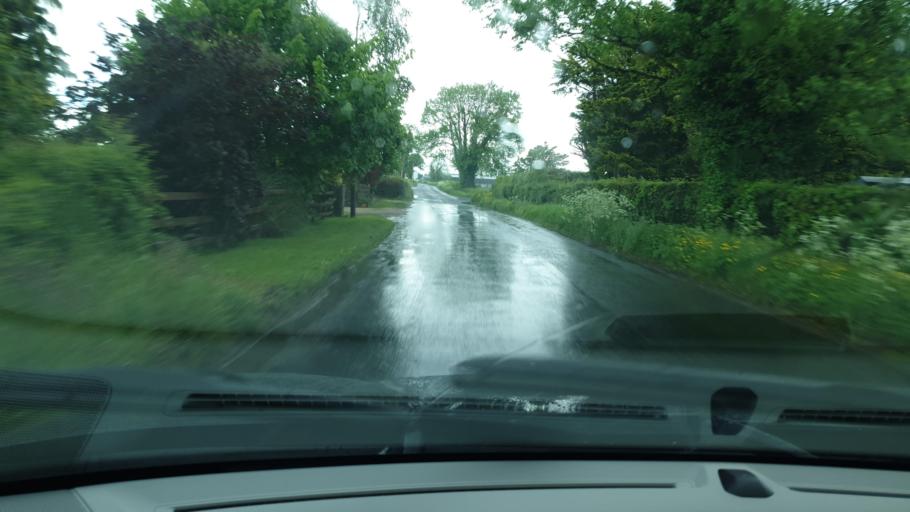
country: IE
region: Leinster
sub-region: Laois
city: Mountmellick
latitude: 53.1041
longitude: -7.3930
